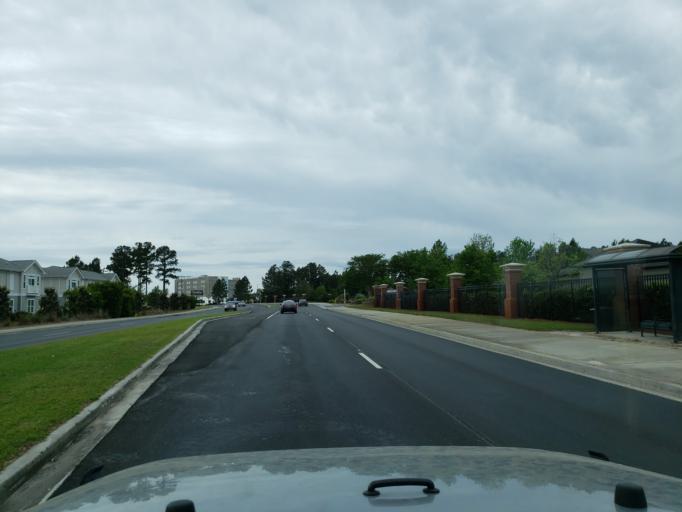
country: US
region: Georgia
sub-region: Chatham County
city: Pooler
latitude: 32.1487
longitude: -81.2465
